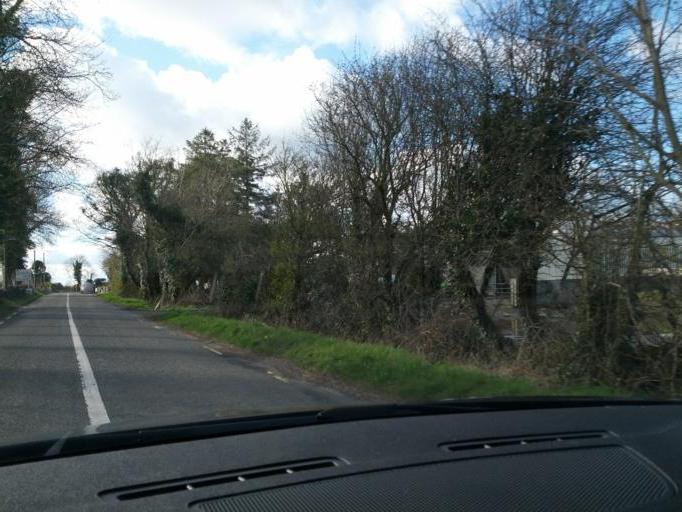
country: IE
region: Connaught
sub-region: Roscommon
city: Castlerea
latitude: 53.5146
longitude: -8.5773
